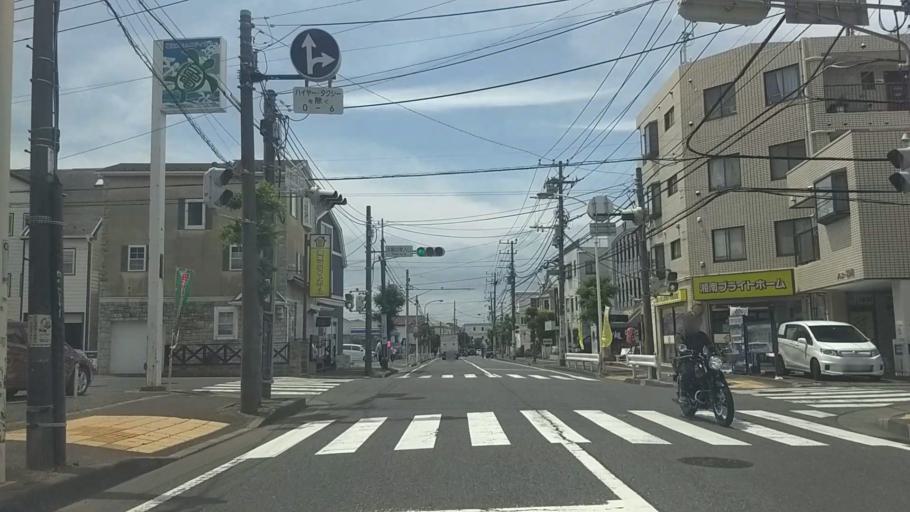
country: JP
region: Kanagawa
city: Fujisawa
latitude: 35.3276
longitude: 139.4679
